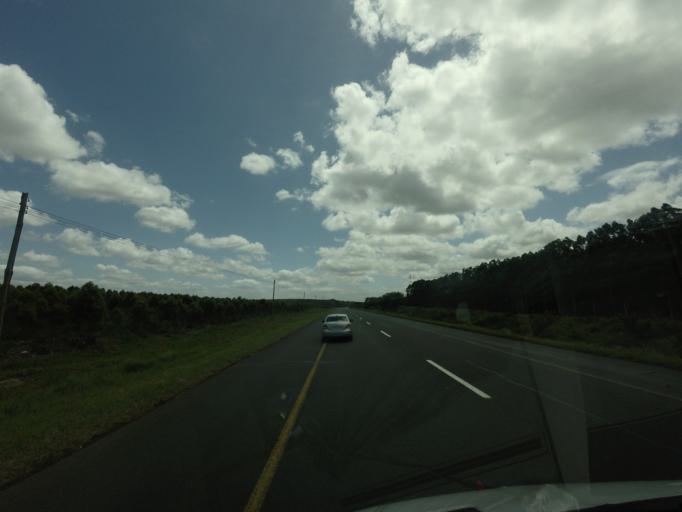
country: ZA
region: KwaZulu-Natal
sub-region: uThungulu District Municipality
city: KwaMbonambi
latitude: -28.5552
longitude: 32.1177
